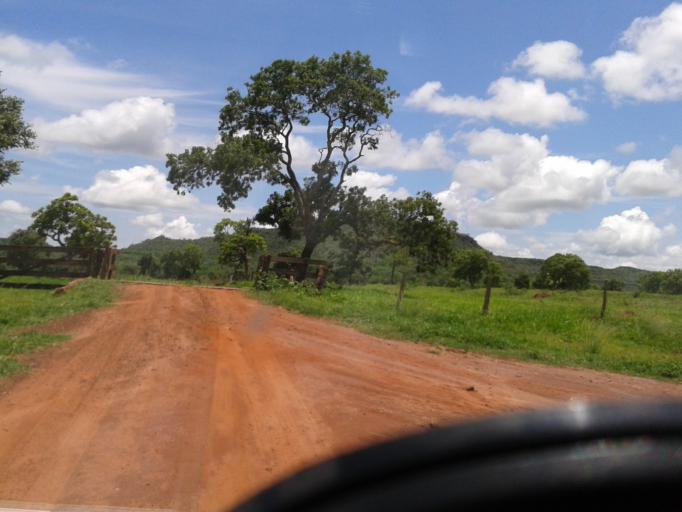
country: BR
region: Minas Gerais
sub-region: Santa Vitoria
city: Santa Vitoria
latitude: -18.9917
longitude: -49.9055
